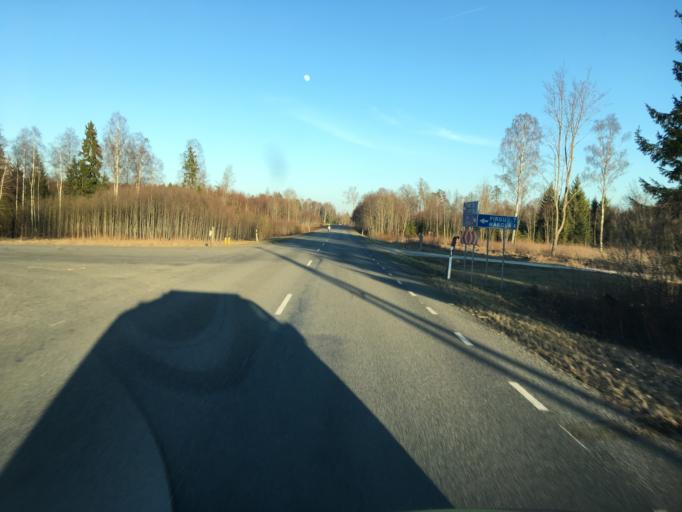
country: EE
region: Raplamaa
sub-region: Rapla vald
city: Rapla
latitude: 59.0716
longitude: 24.9004
